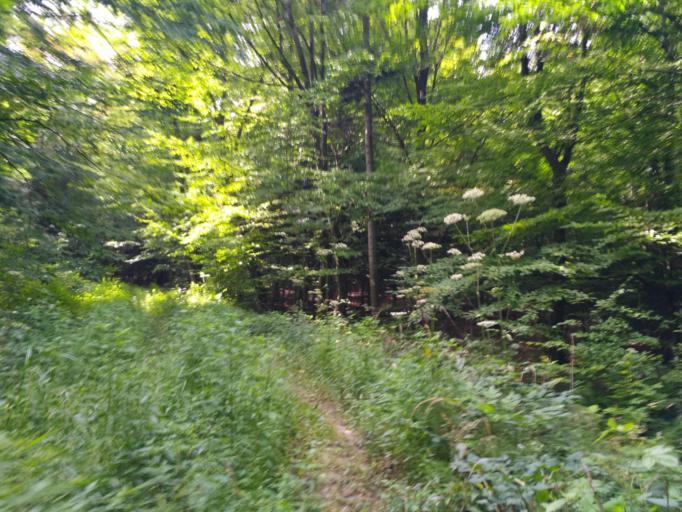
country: PL
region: Subcarpathian Voivodeship
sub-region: Powiat strzyzowski
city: Frysztak
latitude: 49.8888
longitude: 21.5484
